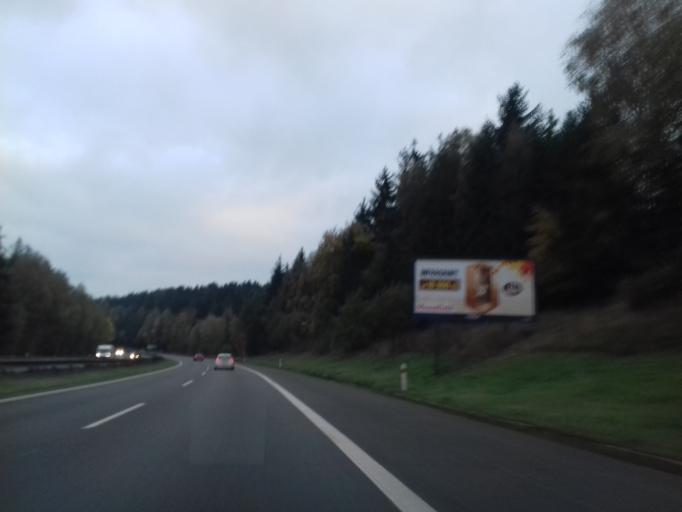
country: CZ
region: Central Bohemia
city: Zruc nad Sazavou
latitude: 49.6944
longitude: 15.0917
